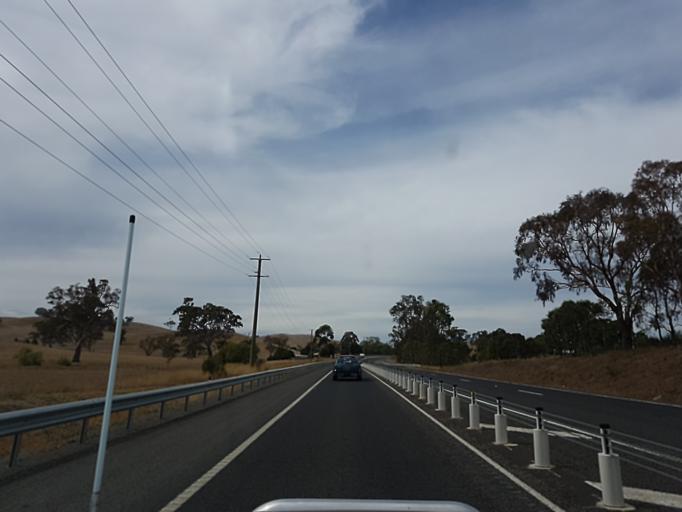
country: AU
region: Victoria
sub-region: Murrindindi
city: Alexandra
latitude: -37.2032
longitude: 145.4637
